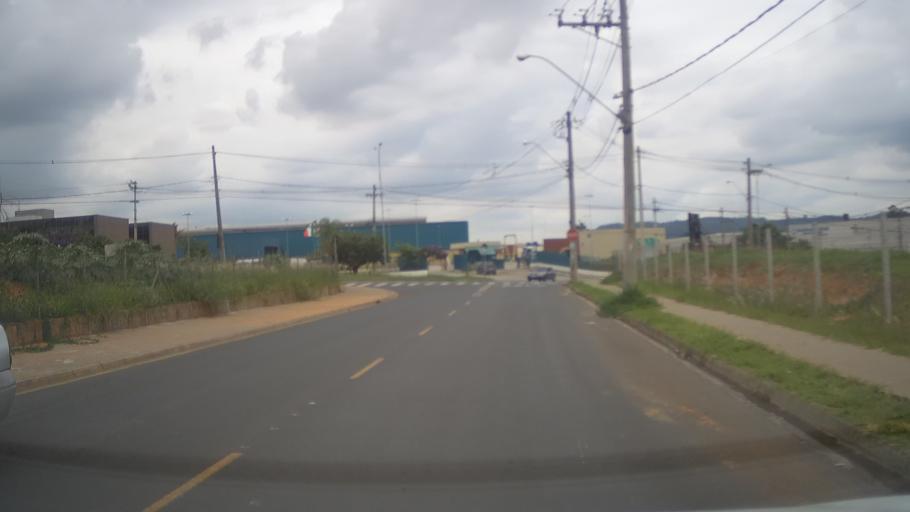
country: BR
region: Sao Paulo
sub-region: Itupeva
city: Itupeva
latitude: -23.1498
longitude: -47.0163
